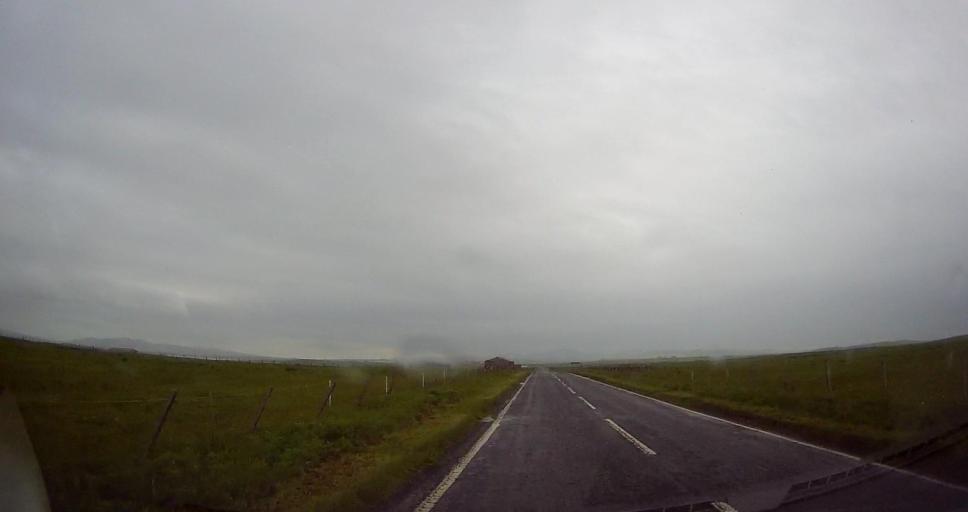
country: GB
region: Scotland
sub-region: Orkney Islands
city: Stromness
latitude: 59.0681
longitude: -3.2803
